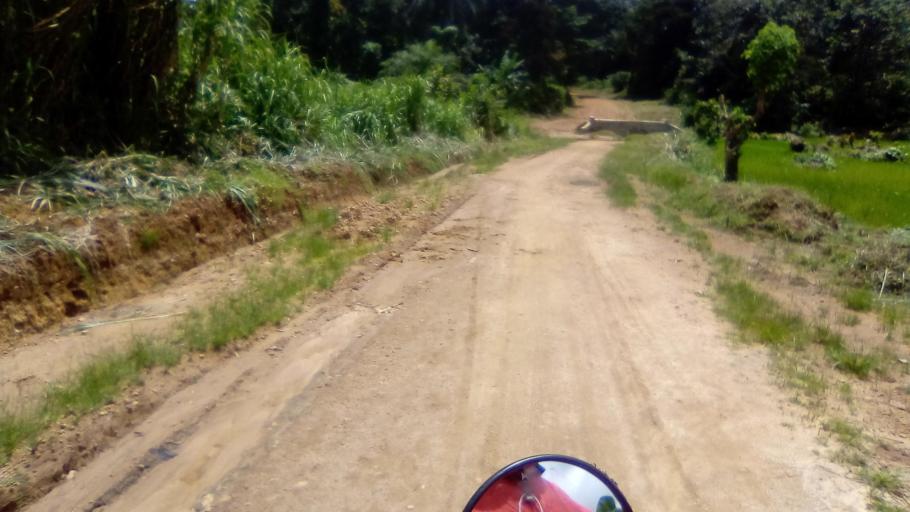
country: SL
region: Eastern Province
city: Giehun
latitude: 8.4998
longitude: -10.9078
